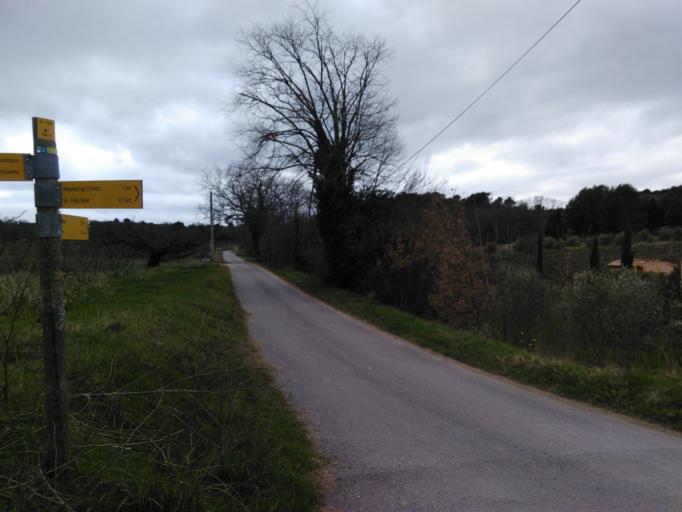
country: FR
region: Provence-Alpes-Cote d'Azur
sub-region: Departement du Vaucluse
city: Malemort-du-Comtat
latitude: 44.0113
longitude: 5.1620
